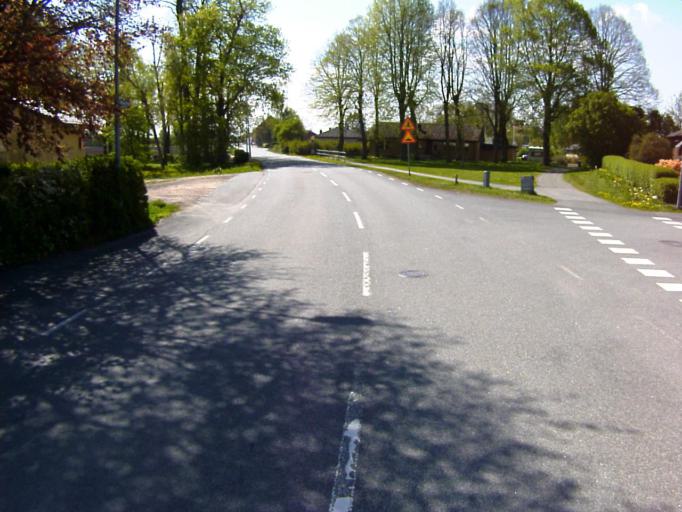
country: SE
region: Skane
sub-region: Kristianstads Kommun
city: Fjalkinge
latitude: 56.0144
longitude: 14.2333
